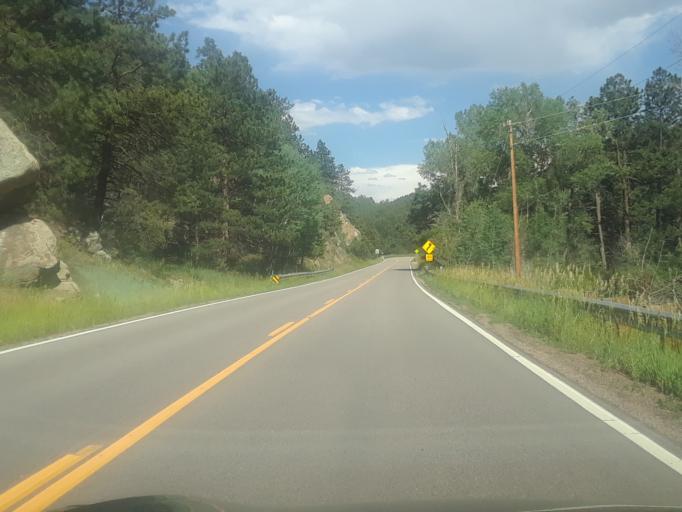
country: US
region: Colorado
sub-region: Jefferson County
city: Kittredge
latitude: 39.7186
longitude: -105.3710
